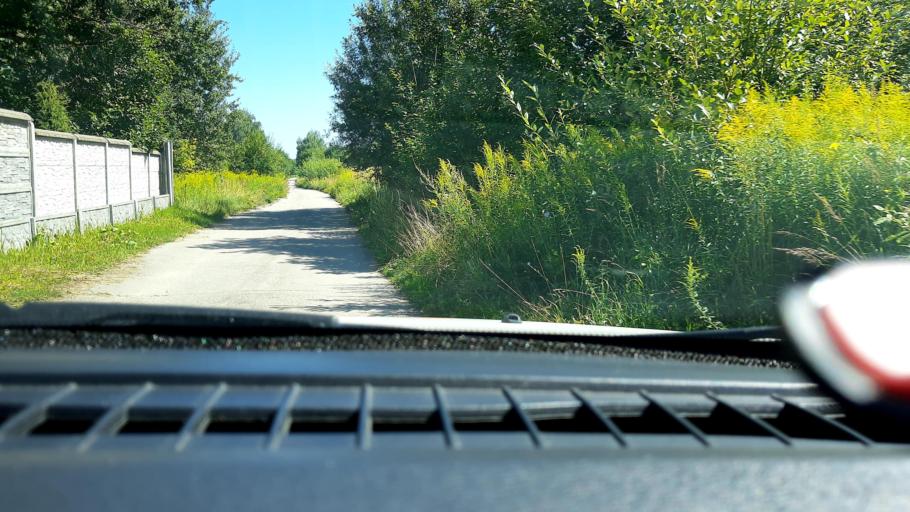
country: RU
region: Nizjnij Novgorod
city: Afonino
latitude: 56.2386
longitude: 44.0357
